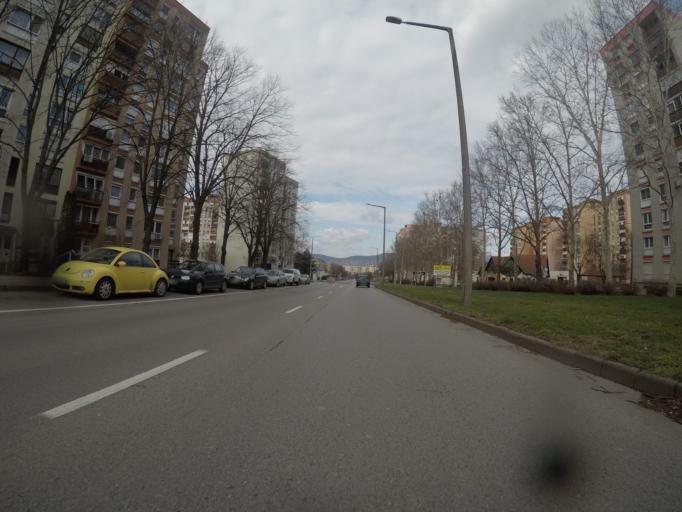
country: HU
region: Baranya
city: Pecs
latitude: 46.0412
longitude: 18.2276
